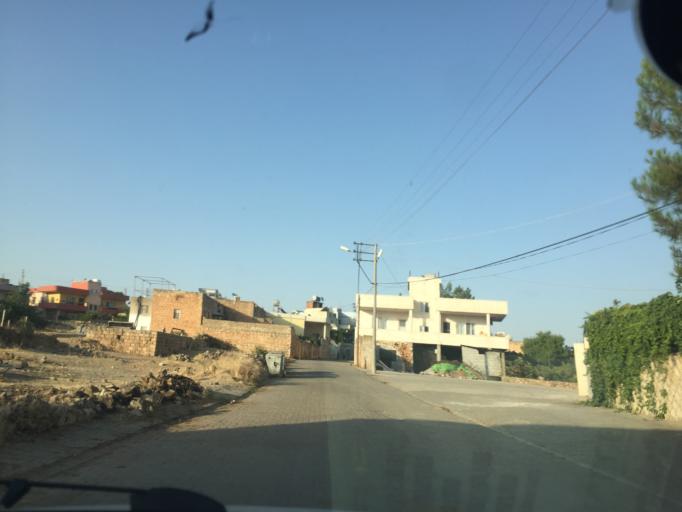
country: TR
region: Mardin
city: Kindirip
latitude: 37.4436
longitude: 41.2149
